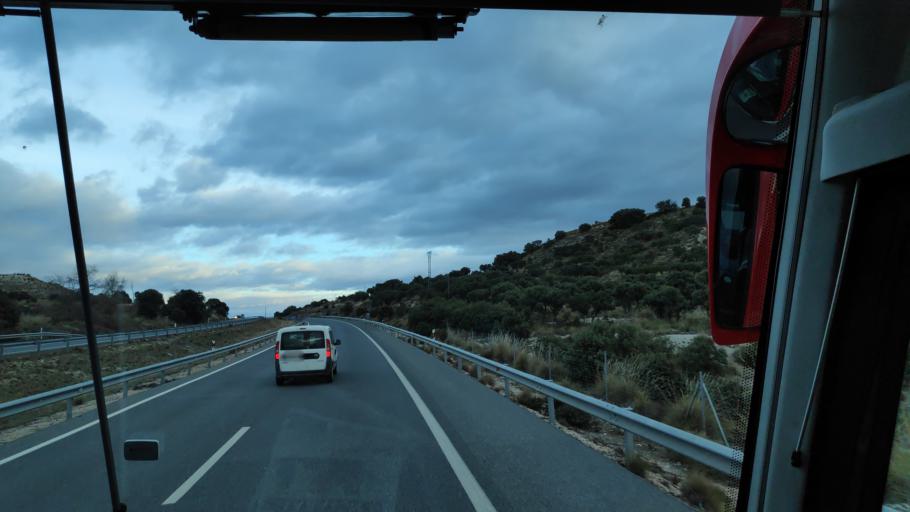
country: ES
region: Madrid
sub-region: Provincia de Madrid
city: Fuentiduena de Tajo
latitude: 40.1412
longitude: -3.2067
